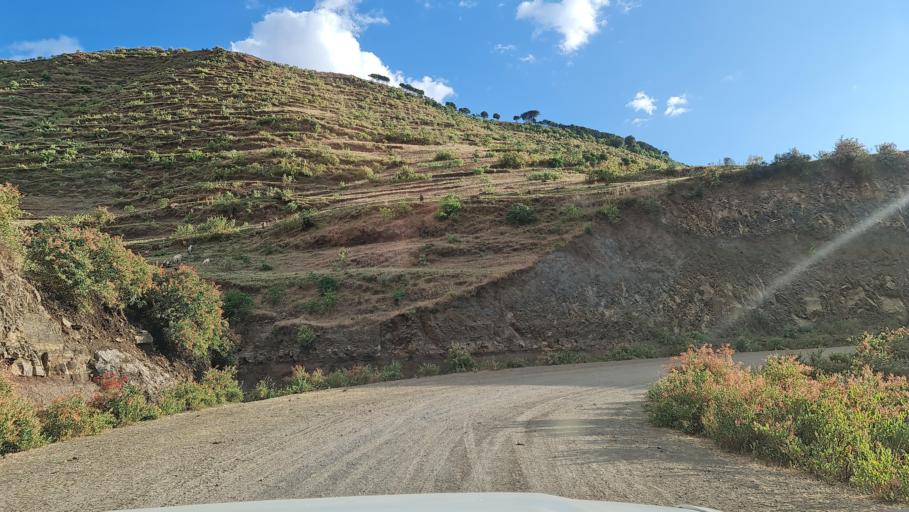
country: ET
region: Amhara
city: Debark'
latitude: 13.0484
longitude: 38.0216
